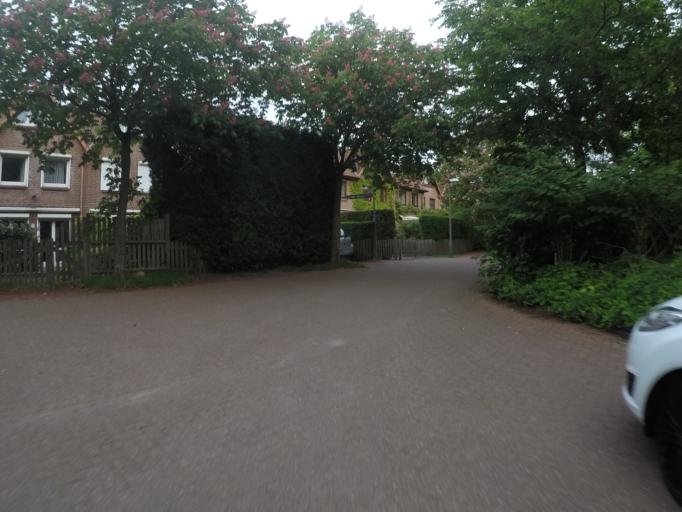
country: DE
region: Schleswig-Holstein
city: Bonningstedt
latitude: 53.6444
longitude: 9.9475
